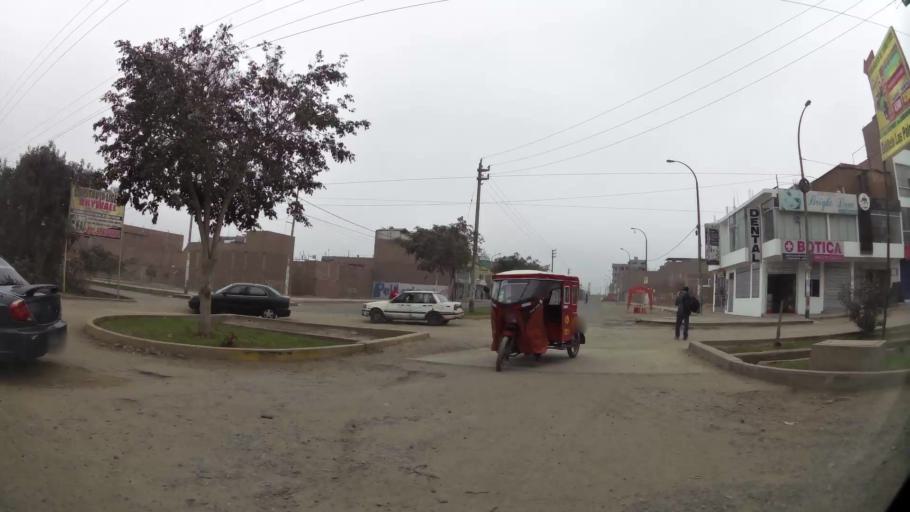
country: PE
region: Lima
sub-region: Lima
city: Urb. Santo Domingo
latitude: -11.8763
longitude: -77.0320
